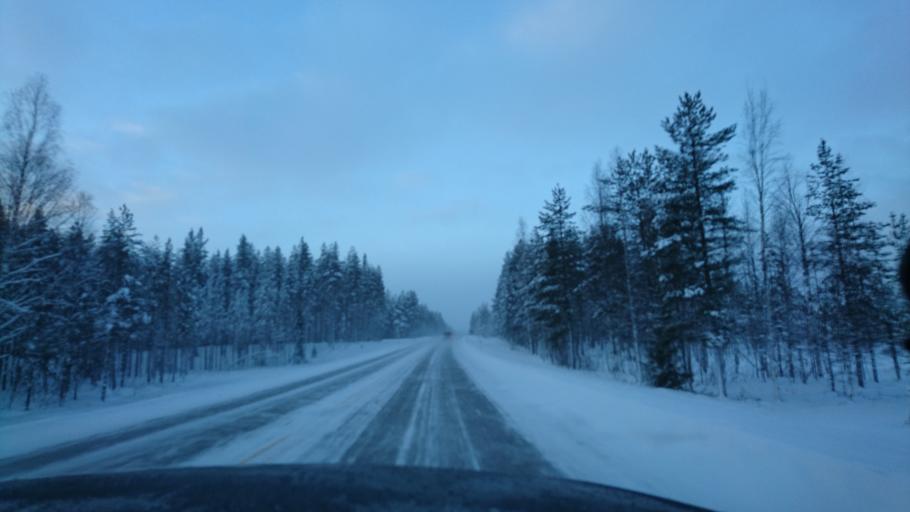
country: FI
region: Northern Ostrobothnia
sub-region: Koillismaa
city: Taivalkoski
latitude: 65.4861
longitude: 27.8447
